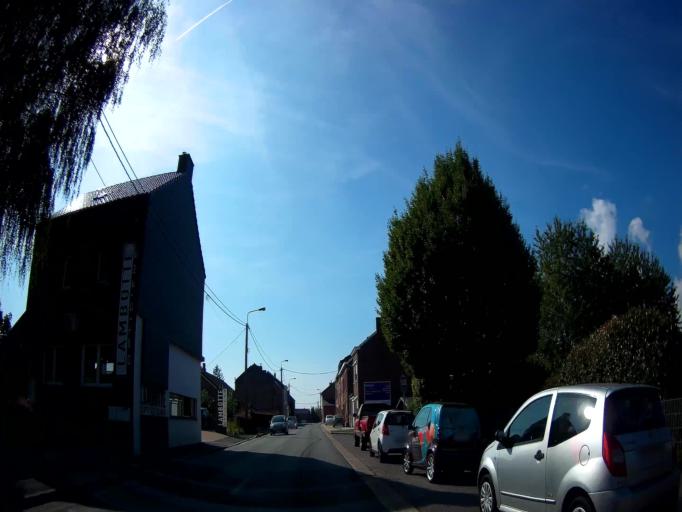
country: BE
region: Wallonia
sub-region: Province de Liege
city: Amay
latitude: 50.5561
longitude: 5.3062
